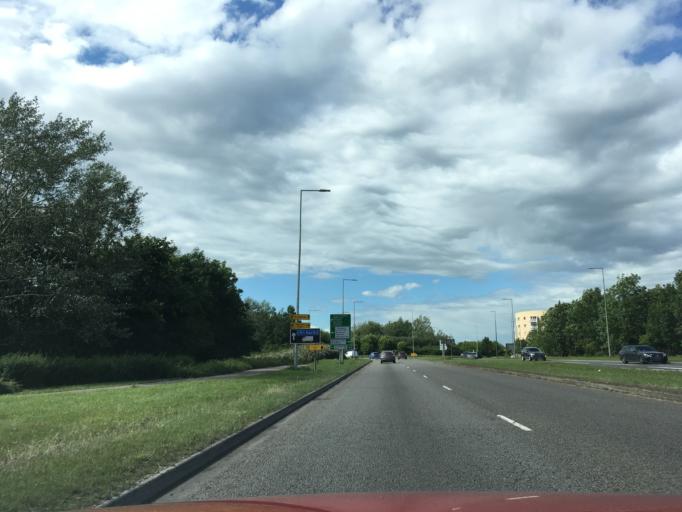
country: GB
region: England
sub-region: Milton Keynes
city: Broughton
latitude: 52.0387
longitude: -0.6931
